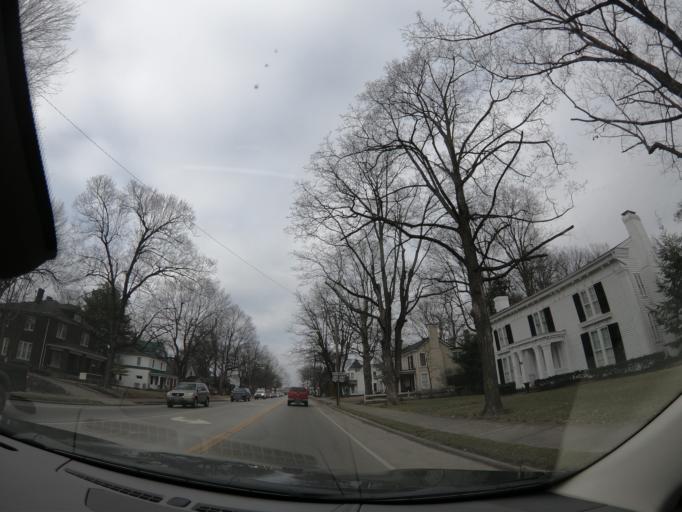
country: US
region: Kentucky
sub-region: Nelson County
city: Bardstown
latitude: 37.8149
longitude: -85.4650
